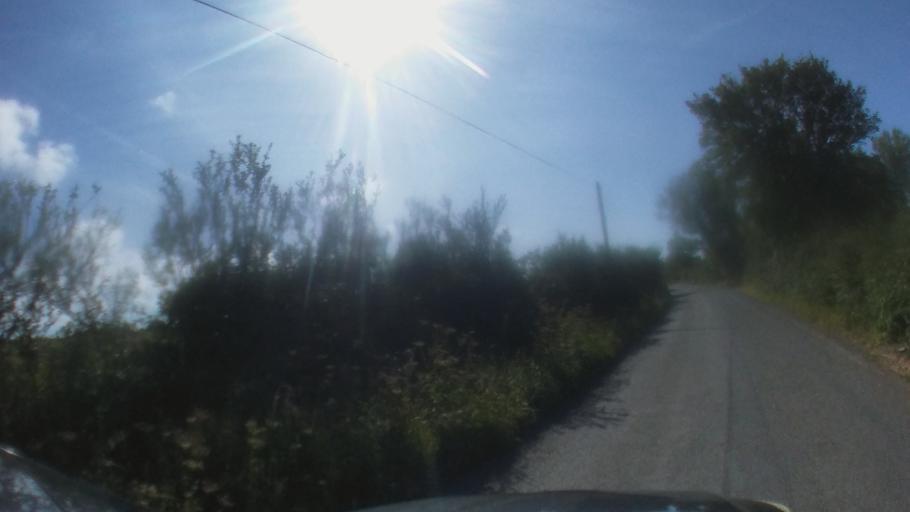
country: IE
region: Leinster
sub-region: Loch Garman
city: Loch Garman
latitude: 52.2265
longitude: -6.5480
